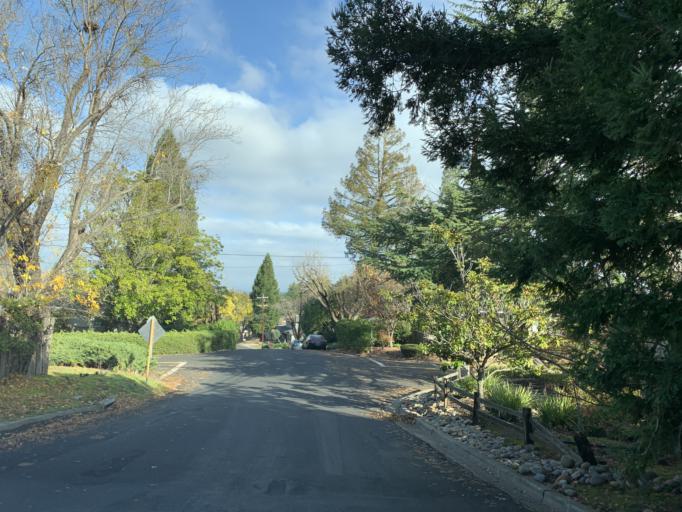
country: US
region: California
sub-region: Contra Costa County
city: Saranap
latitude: 37.8837
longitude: -122.0687
